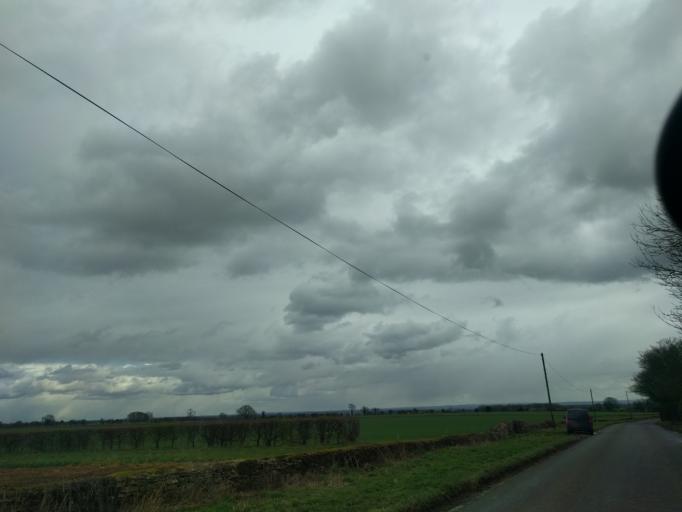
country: GB
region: England
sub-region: Gloucestershire
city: Nailsworth
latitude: 51.6492
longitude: -2.2537
